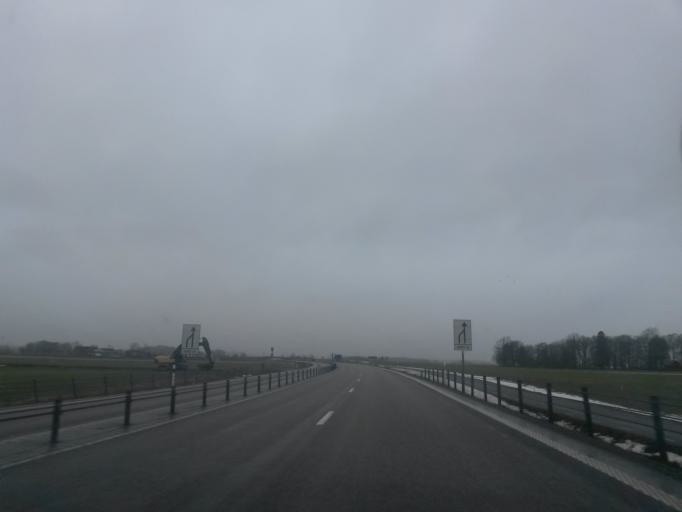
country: SE
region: Vaestra Goetaland
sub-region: Vanersborgs Kommun
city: Vargon
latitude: 58.2940
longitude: 12.3843
